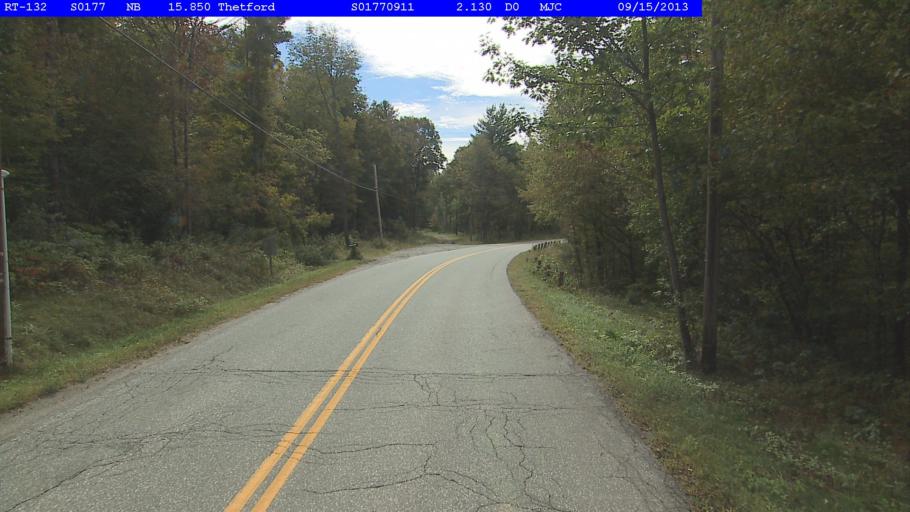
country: US
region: New Hampshire
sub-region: Grafton County
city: Hanover
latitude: 43.8246
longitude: -72.2855
